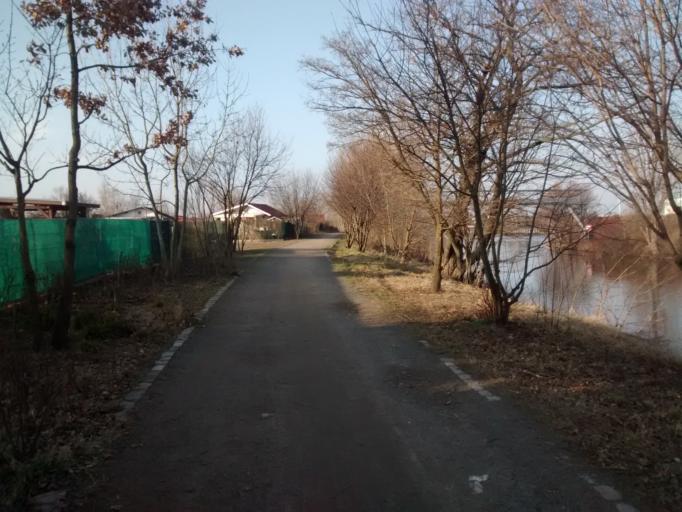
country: DE
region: Berlin
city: Charlottenburg-Nord
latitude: 52.5325
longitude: 13.3126
